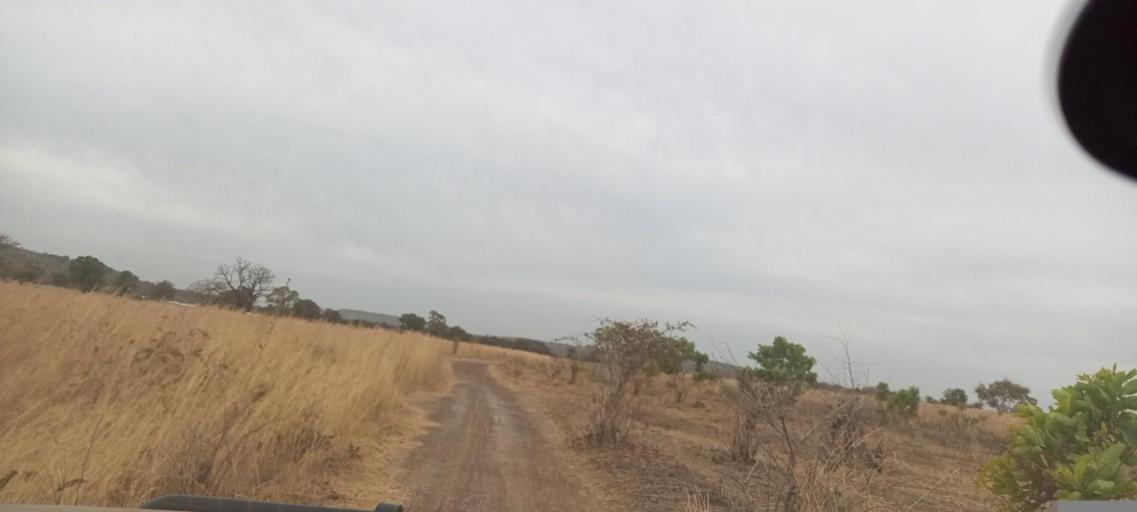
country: ML
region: Koulikoro
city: Kati
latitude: 12.7652
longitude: -8.4001
